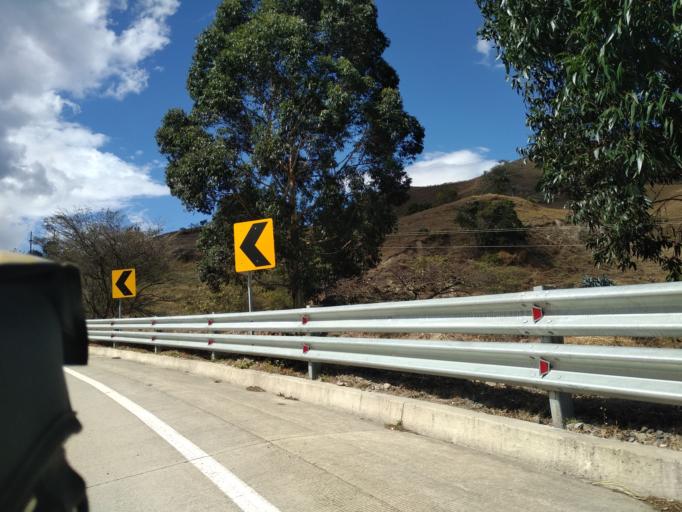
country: EC
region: Loja
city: Loja
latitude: -4.3475
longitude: -79.1914
